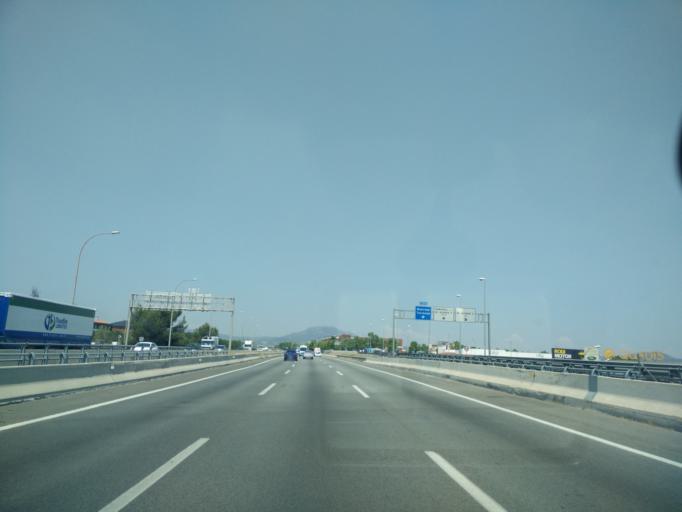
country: ES
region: Catalonia
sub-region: Provincia de Barcelona
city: Sant Quirze del Valles
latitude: 41.5305
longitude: 2.0929
